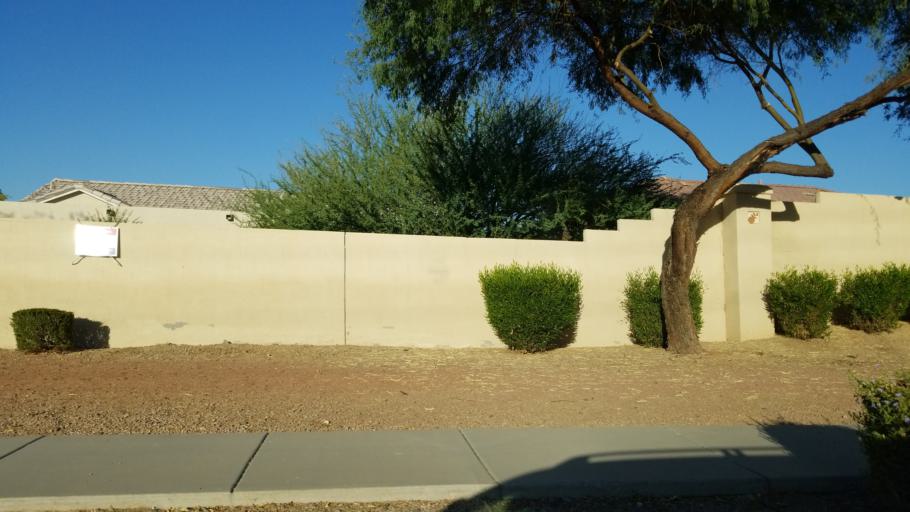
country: US
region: Arizona
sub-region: Maricopa County
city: Laveen
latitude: 33.3584
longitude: -112.1176
